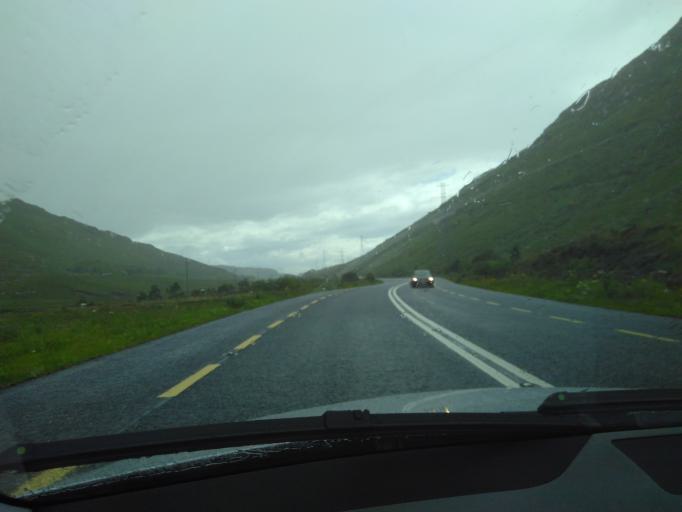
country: IE
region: Ulster
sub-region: County Donegal
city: Donegal
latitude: 54.7195
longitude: -7.9546
